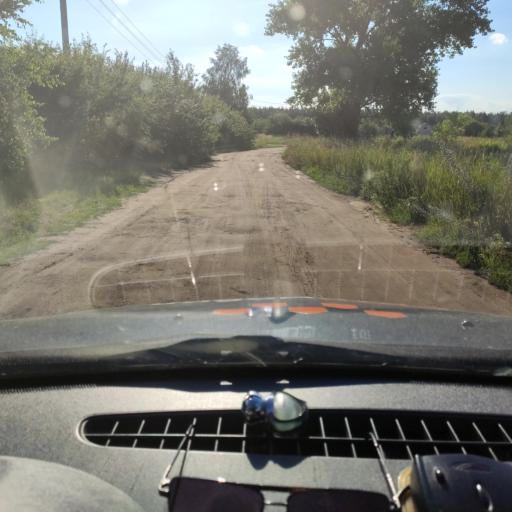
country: RU
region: Voronezj
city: Podgornoye
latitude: 51.8647
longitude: 39.1759
